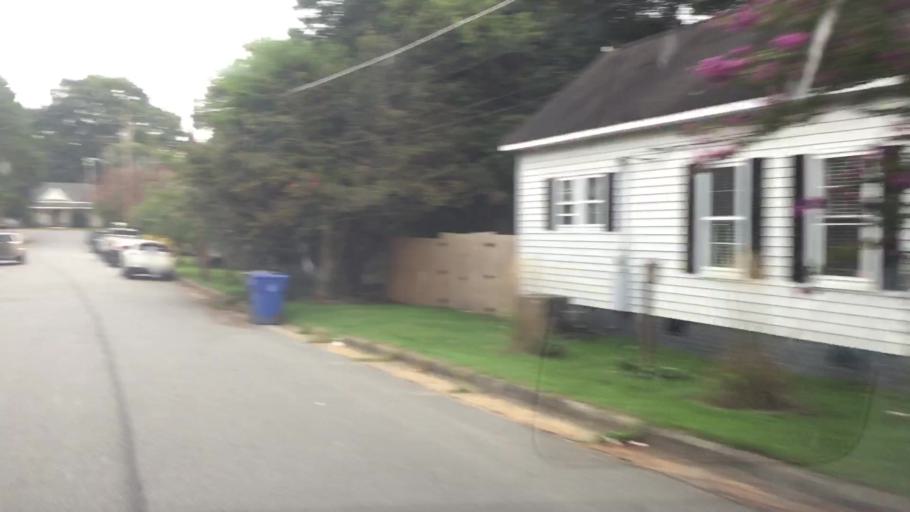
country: US
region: North Carolina
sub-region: Iredell County
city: Mooresville
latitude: 35.5751
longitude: -80.8163
